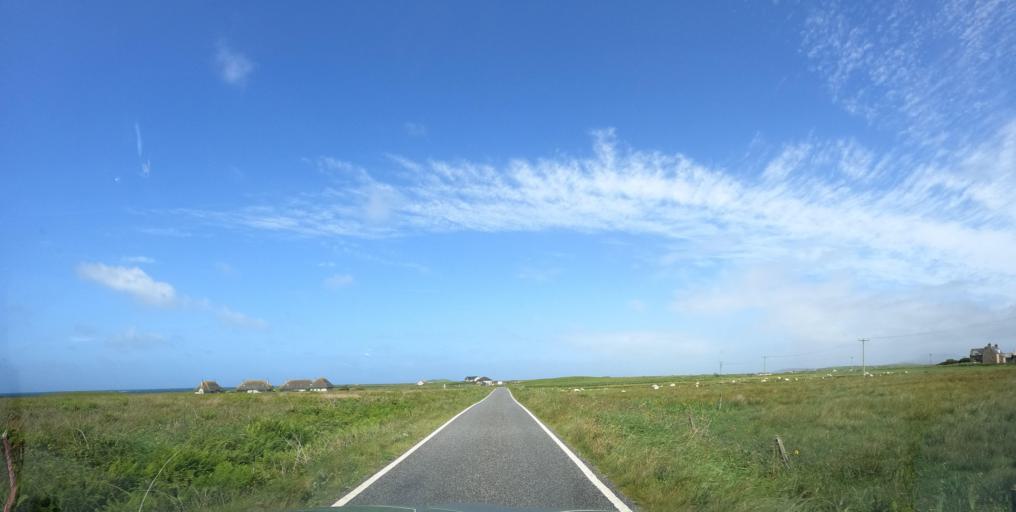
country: GB
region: Scotland
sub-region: Eilean Siar
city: Isle of South Uist
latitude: 57.1081
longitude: -7.3710
